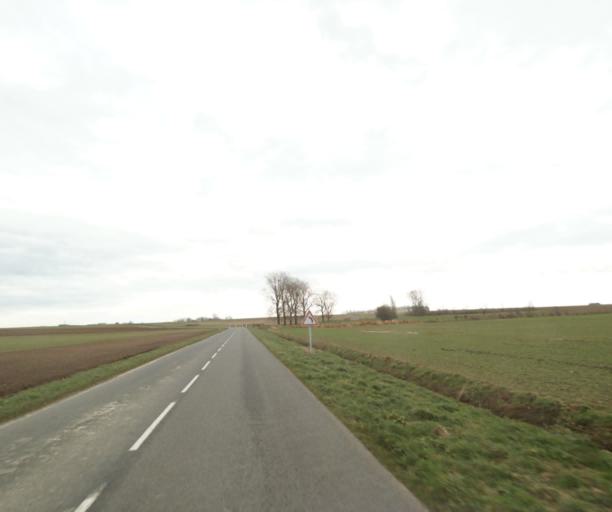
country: FR
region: Nord-Pas-de-Calais
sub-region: Departement du Nord
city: Curgies
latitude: 50.3305
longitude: 3.6172
